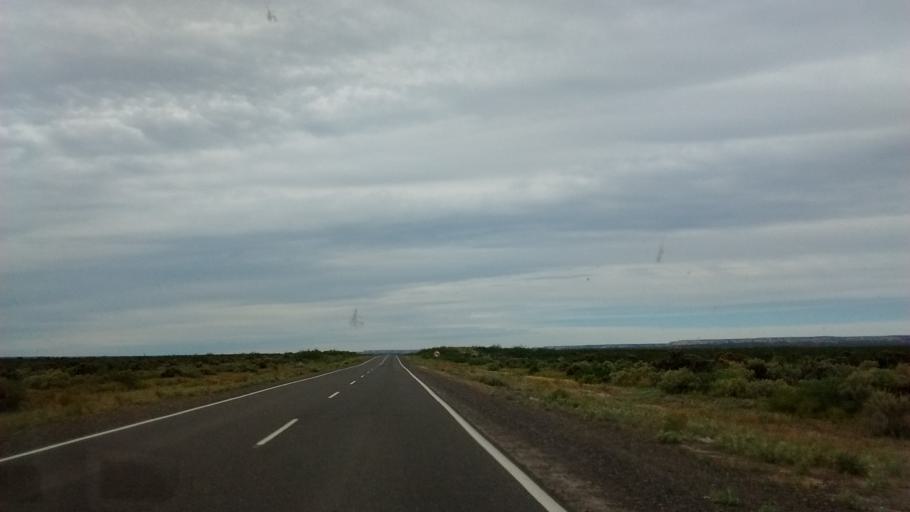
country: AR
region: Rio Negro
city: Catriel
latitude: -38.0822
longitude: -67.9250
